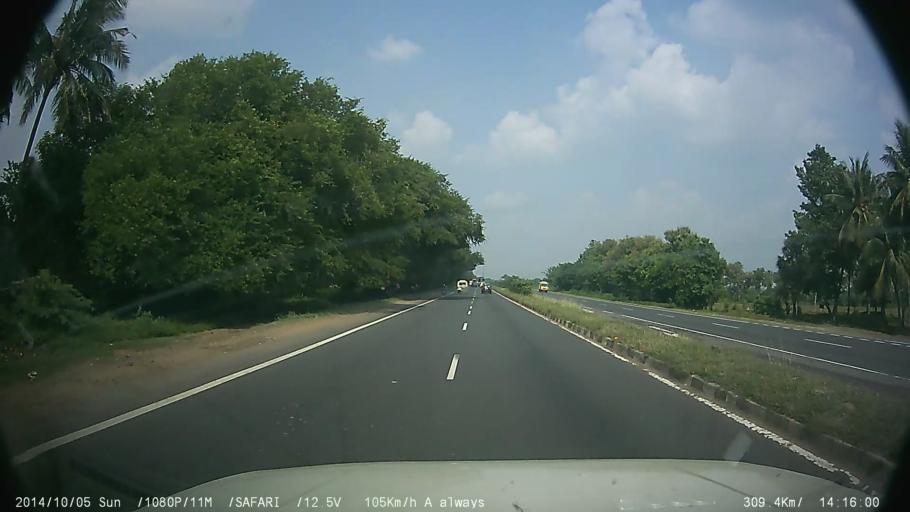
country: IN
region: Tamil Nadu
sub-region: Villupuram
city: Tindivanam
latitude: 12.2817
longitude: 79.7078
